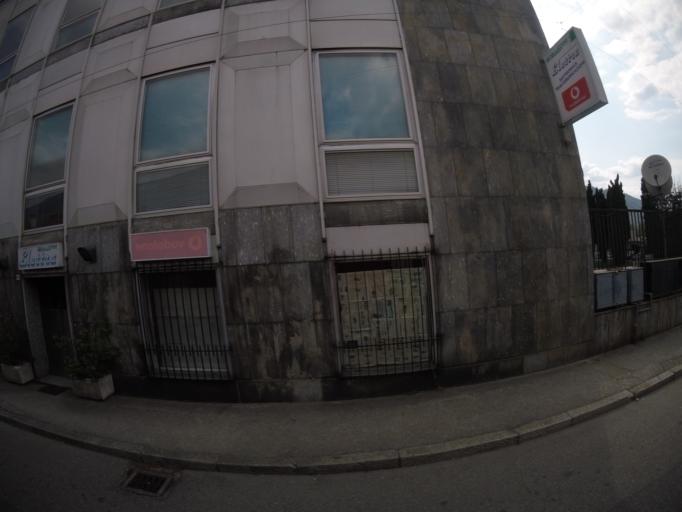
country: IT
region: Piedmont
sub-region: Provincia Verbano-Cusio-Ossola
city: Omegna
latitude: 45.8896
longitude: 8.4095
